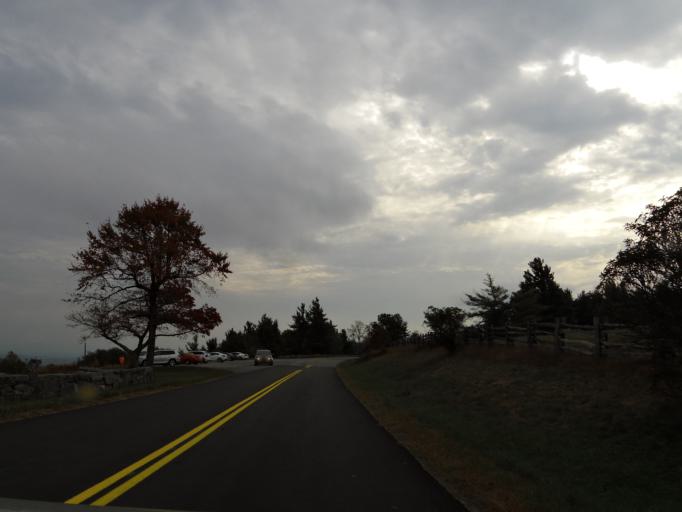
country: US
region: North Carolina
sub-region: Alleghany County
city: Sparta
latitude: 36.4093
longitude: -81.1956
